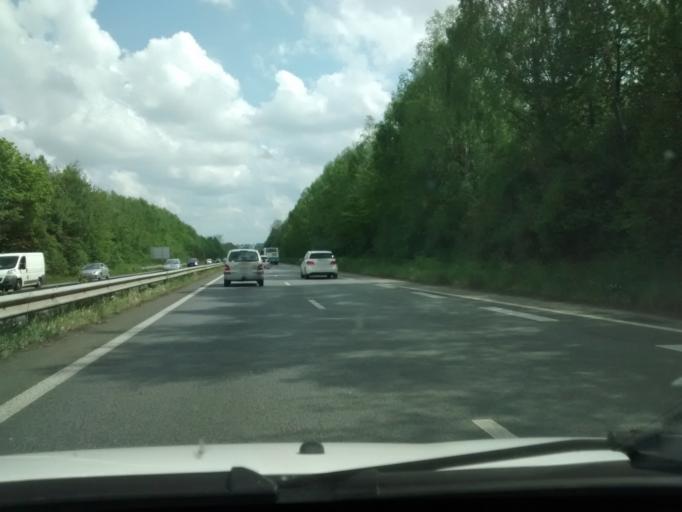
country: FR
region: Brittany
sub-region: Departement d'Ille-et-Vilaine
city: Montgermont
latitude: 48.1716
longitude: -1.7148
